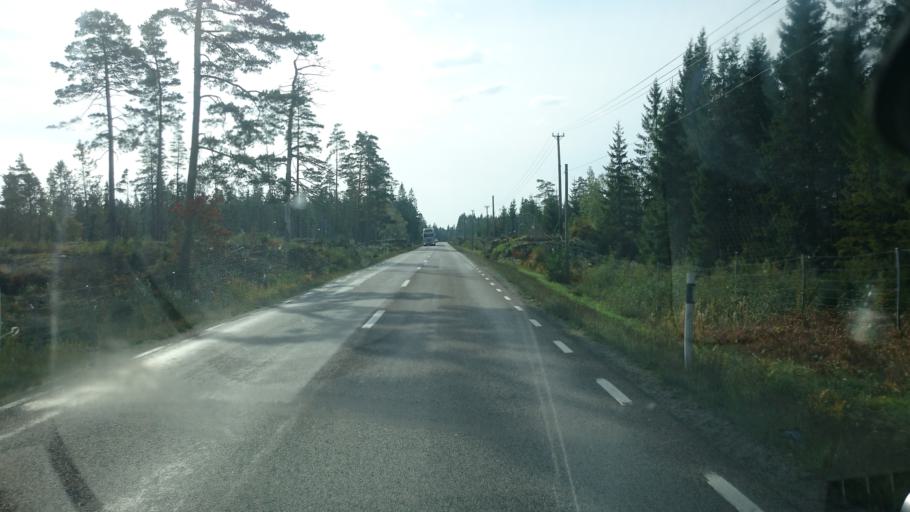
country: SE
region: Vaestra Goetaland
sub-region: Alingsas Kommun
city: Sollebrunn
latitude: 58.1992
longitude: 12.4308
